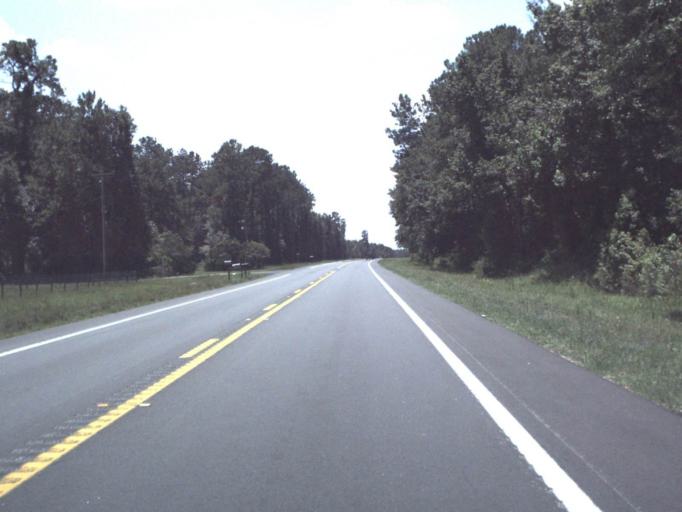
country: US
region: Florida
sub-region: Alachua County
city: Alachua
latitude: 29.8971
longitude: -82.4227
